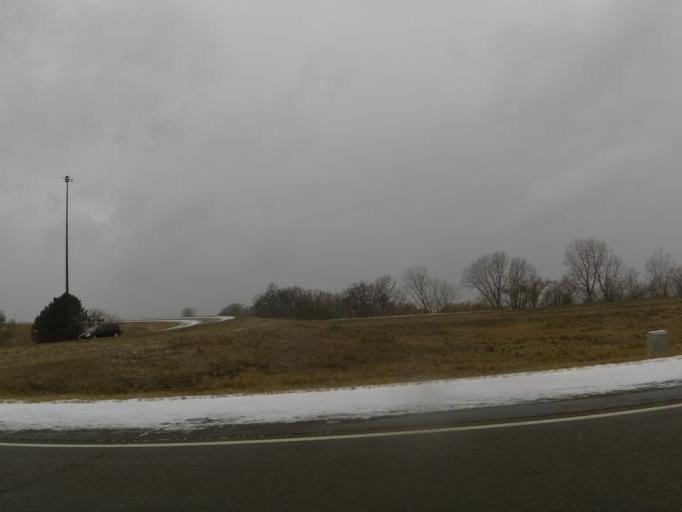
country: US
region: Minnesota
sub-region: Dakota County
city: Eagan
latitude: 44.8165
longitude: -93.2222
